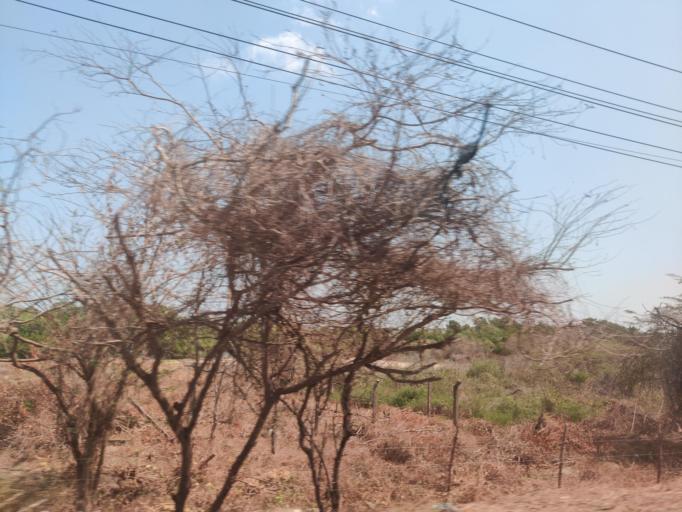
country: CO
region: Bolivar
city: Turbana
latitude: 10.2747
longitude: -75.5415
